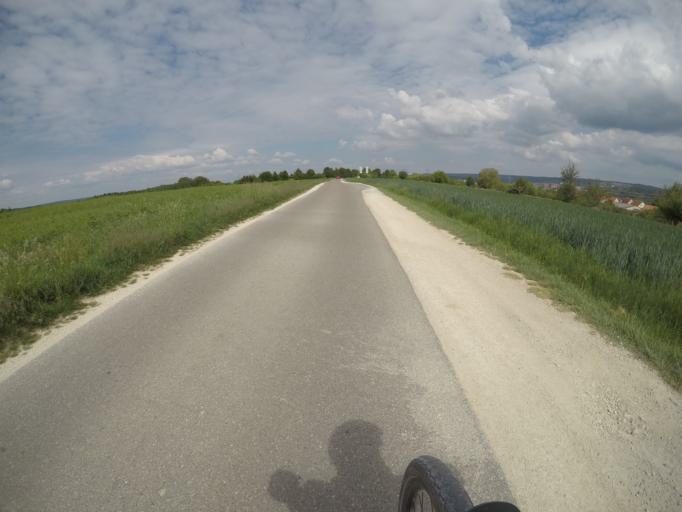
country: DE
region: Baden-Wuerttemberg
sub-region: Regierungsbezirk Stuttgart
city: Notzingen
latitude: 48.6678
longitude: 9.4307
